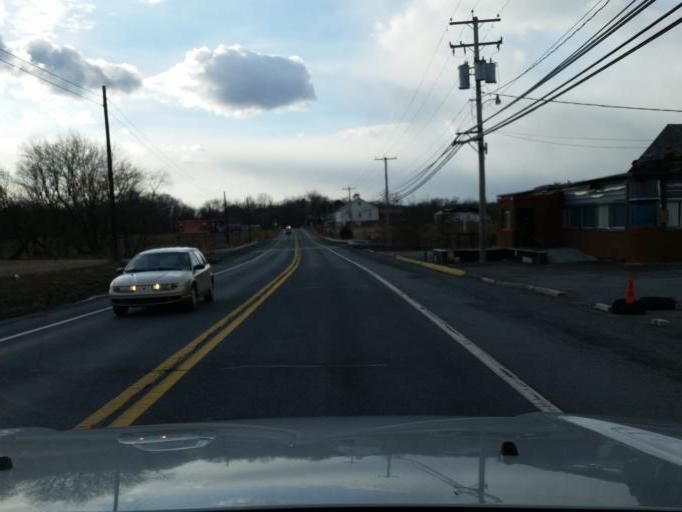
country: US
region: Pennsylvania
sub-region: Dauphin County
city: Middletown
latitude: 40.1980
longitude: -76.7107
